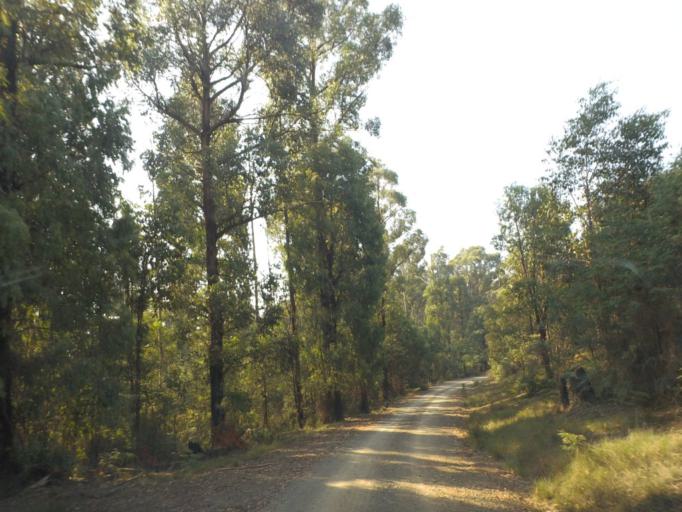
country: AU
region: Victoria
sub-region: Yarra Ranges
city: Millgrove
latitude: -37.5288
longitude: 145.7414
